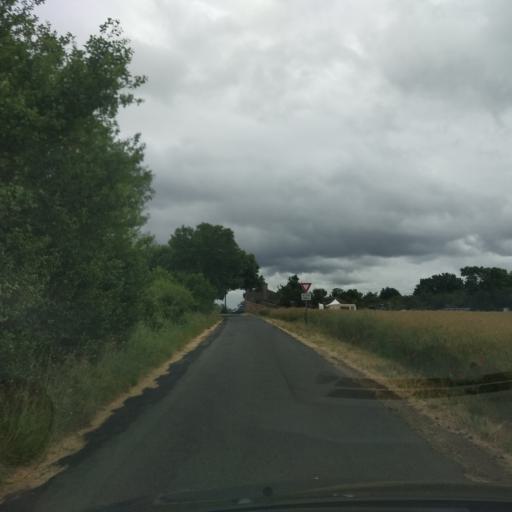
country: FR
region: Poitou-Charentes
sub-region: Departement de la Vienne
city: Vouneuil-sous-Biard
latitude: 46.5955
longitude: 0.2779
